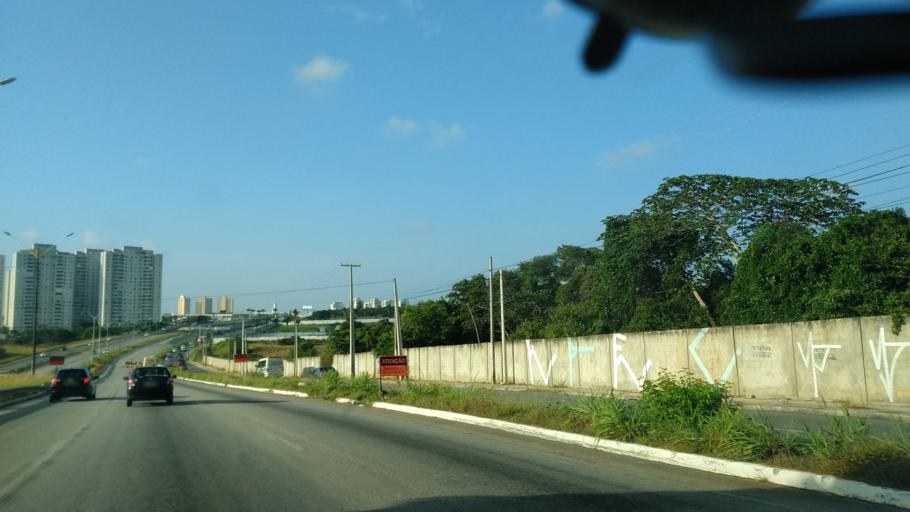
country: BR
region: Rio Grande do Norte
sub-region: Parnamirim
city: Parnamirim
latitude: -5.8825
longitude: -35.2259
